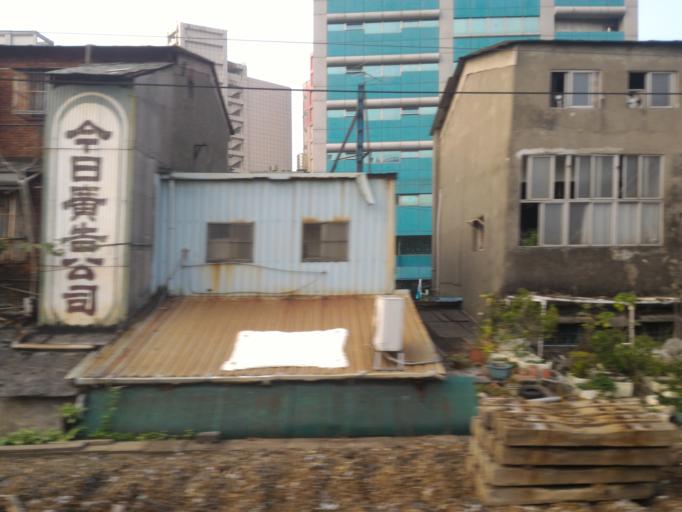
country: TW
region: Taiwan
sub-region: Taoyuan
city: Taoyuan
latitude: 24.9899
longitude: 121.3170
